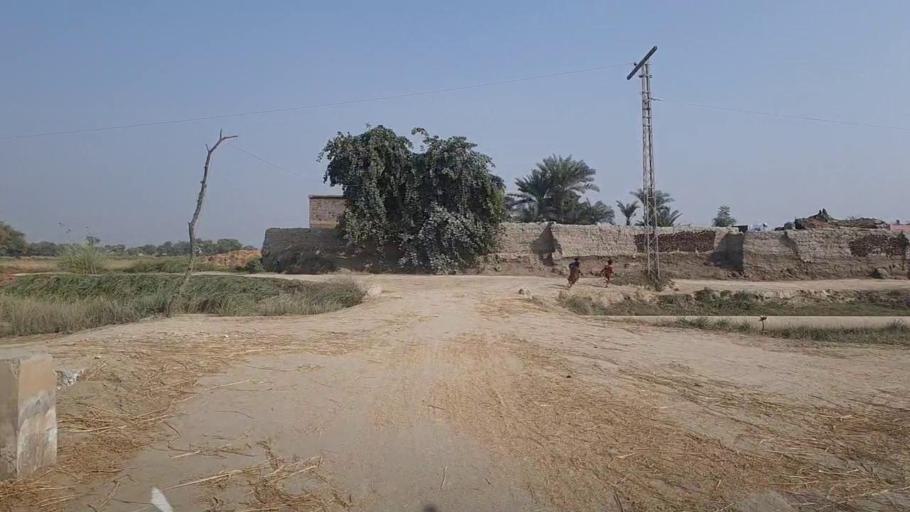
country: PK
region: Sindh
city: Kandhkot
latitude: 28.2337
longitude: 69.2216
